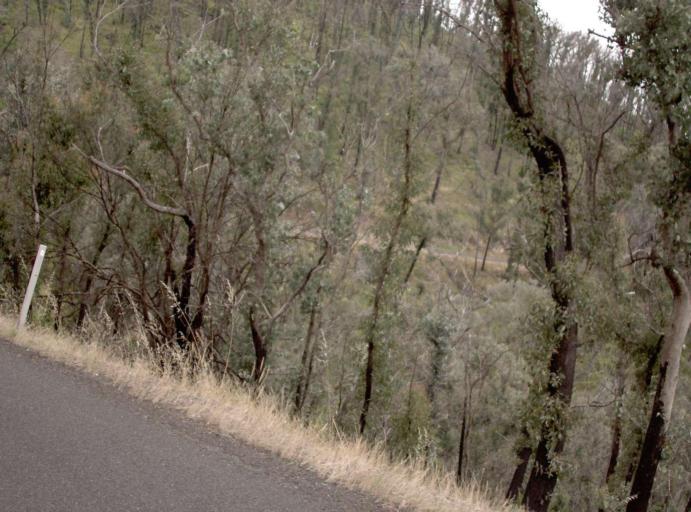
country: AU
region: Victoria
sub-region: Wellington
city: Heyfield
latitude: -37.8165
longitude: 146.6723
